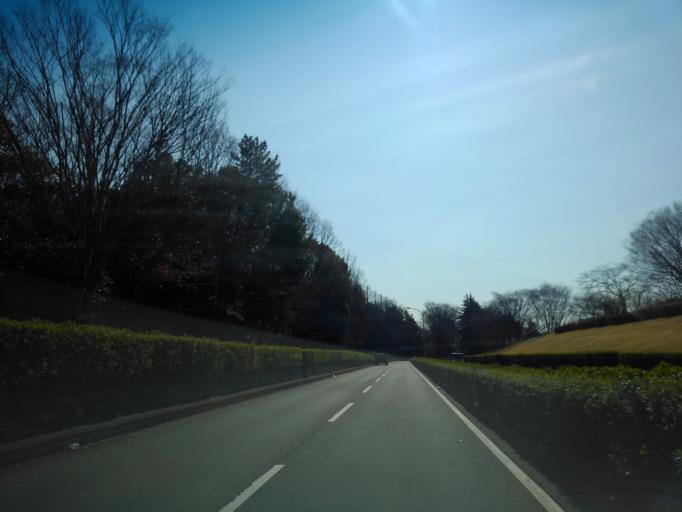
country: JP
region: Saitama
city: Tokorozawa
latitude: 35.7974
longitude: 139.4693
